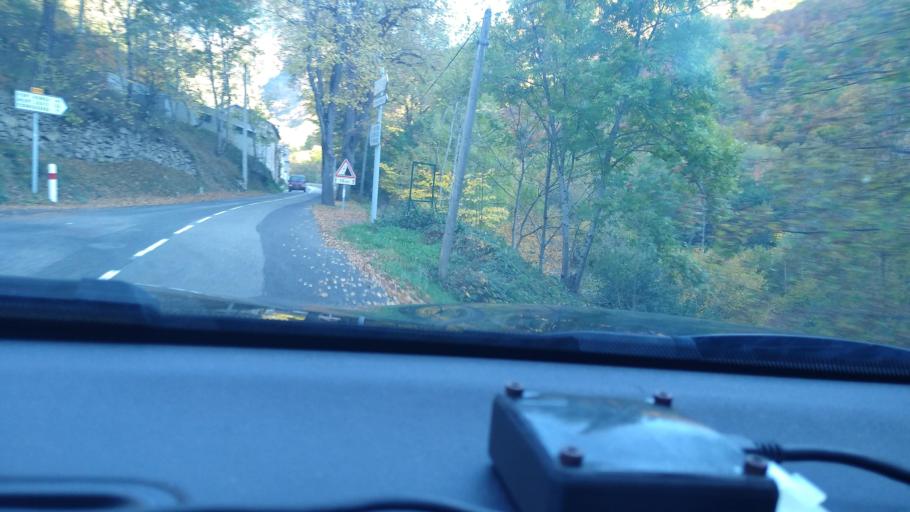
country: FR
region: Languedoc-Roussillon
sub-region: Departement de l'Aude
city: Quillan
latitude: 42.7162
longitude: 2.1298
